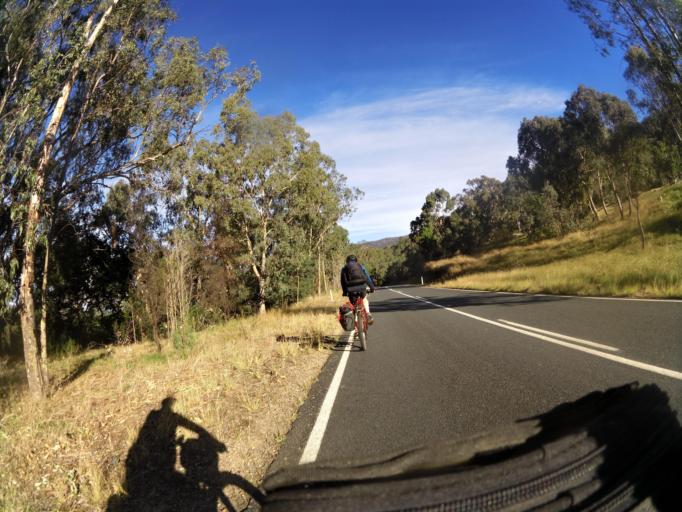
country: AU
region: New South Wales
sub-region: Greater Hume Shire
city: Holbrook
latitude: -35.9766
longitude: 147.8130
